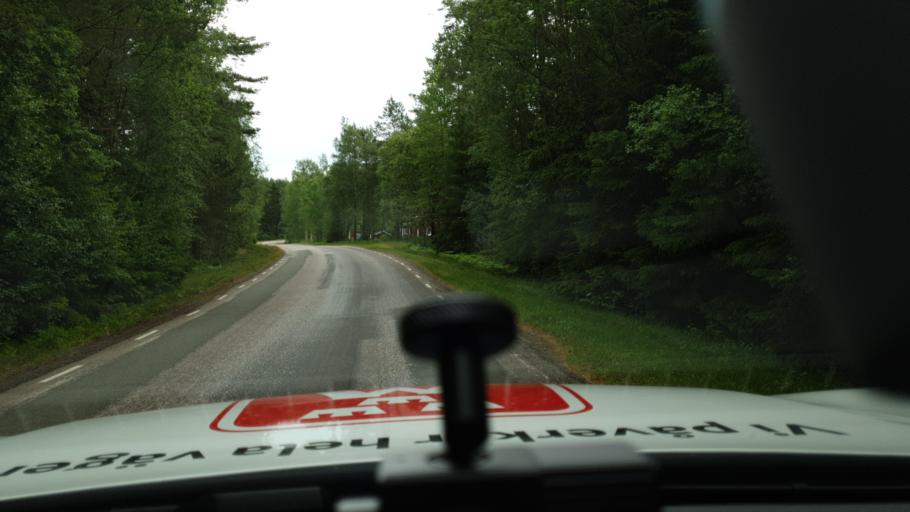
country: SE
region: Vaestra Goetaland
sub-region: Hjo Kommun
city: Hjo
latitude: 58.4068
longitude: 14.2682
